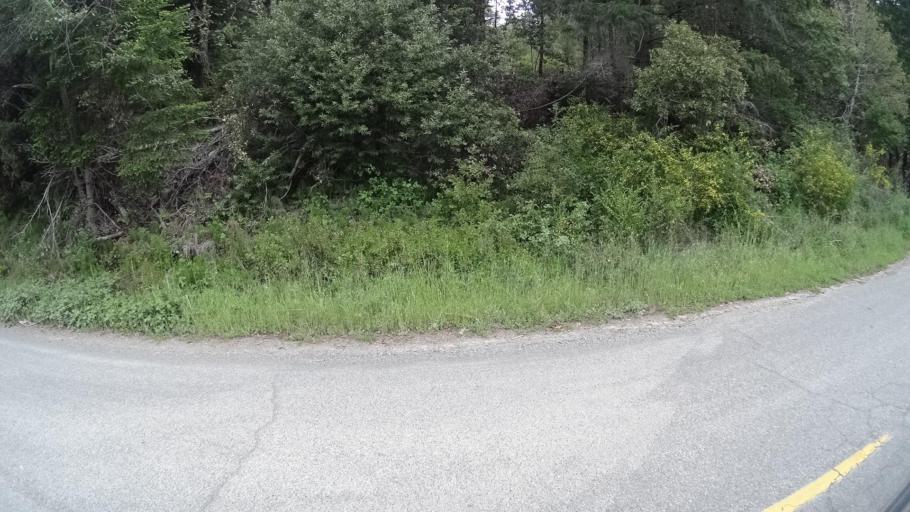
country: US
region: California
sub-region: Humboldt County
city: Redway
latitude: 40.2958
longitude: -123.8308
